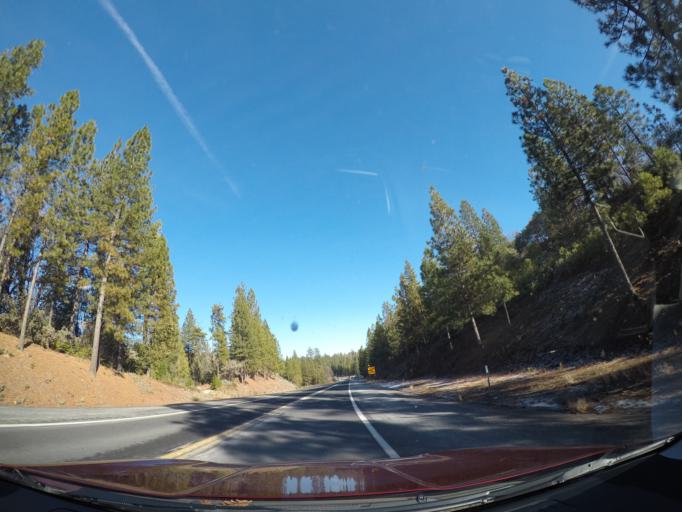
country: US
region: California
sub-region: Tuolumne County
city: Twain Harte
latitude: 38.0375
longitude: -120.2226
